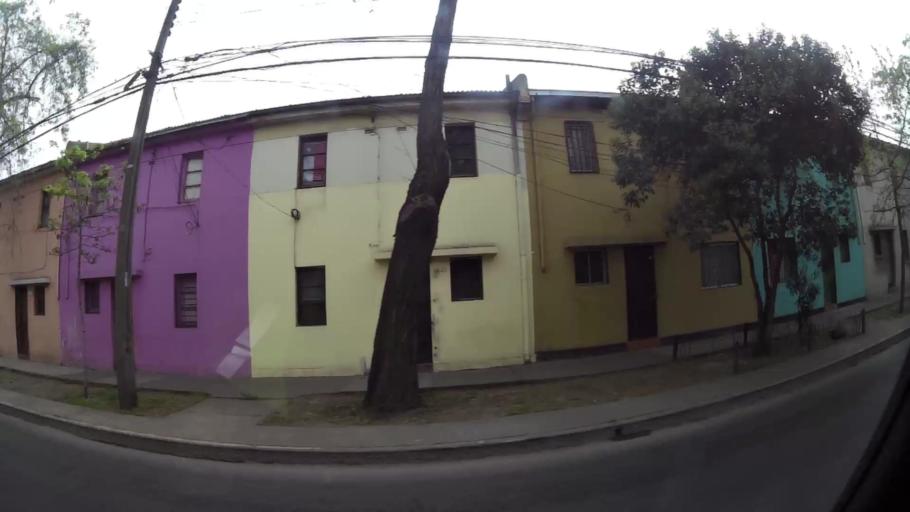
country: CL
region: Santiago Metropolitan
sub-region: Provincia de Santiago
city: Santiago
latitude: -33.4703
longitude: -70.6529
